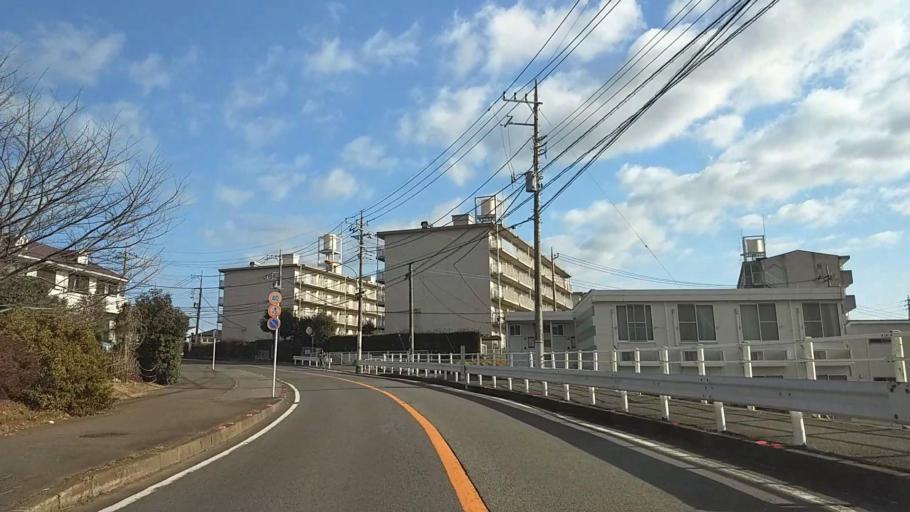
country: JP
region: Kanagawa
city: Atsugi
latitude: 35.4330
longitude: 139.3360
